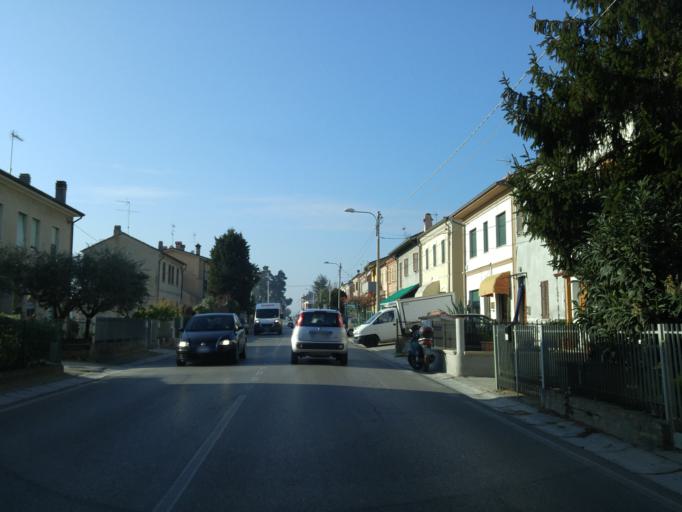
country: IT
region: The Marches
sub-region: Provincia di Pesaro e Urbino
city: Cuccurano
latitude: 43.8046
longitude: 12.9773
